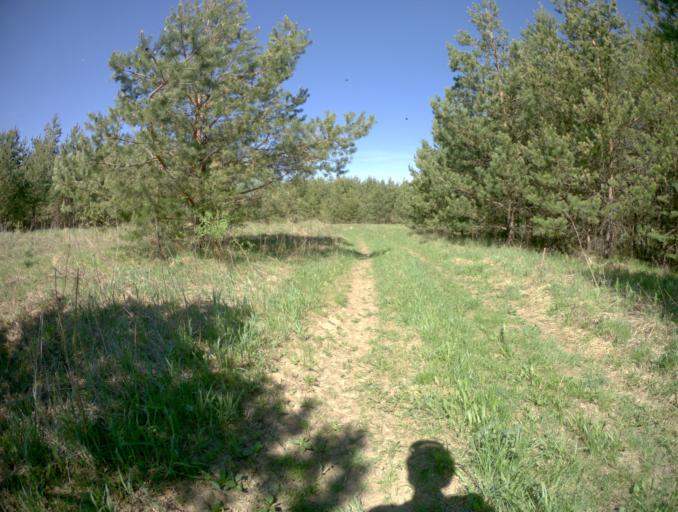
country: RU
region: Ivanovo
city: Gavrilov Posad
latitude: 56.4262
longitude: 40.1997
